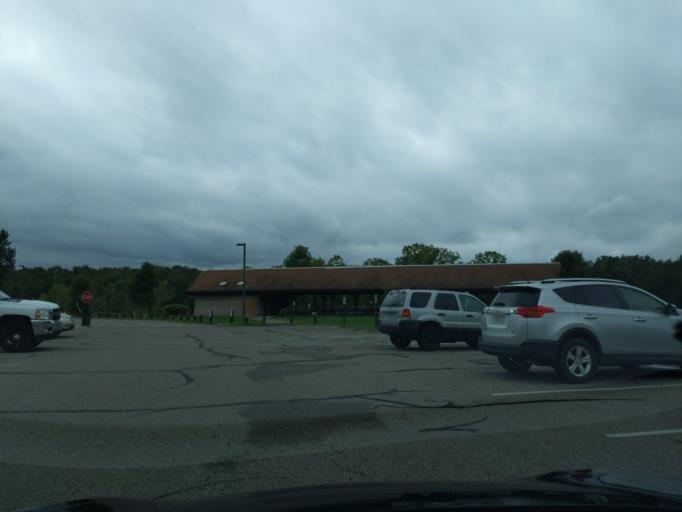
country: US
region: Michigan
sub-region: Ingham County
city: Lansing
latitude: 42.6965
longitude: -84.5285
